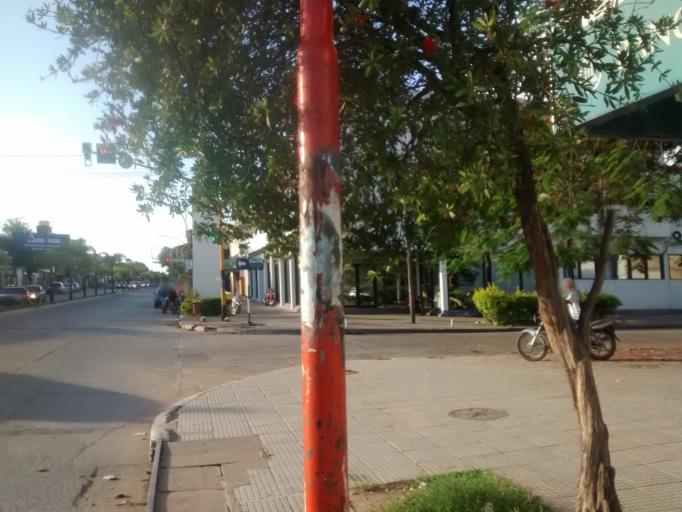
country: AR
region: Chaco
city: Resistencia
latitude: -27.4409
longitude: -58.9980
